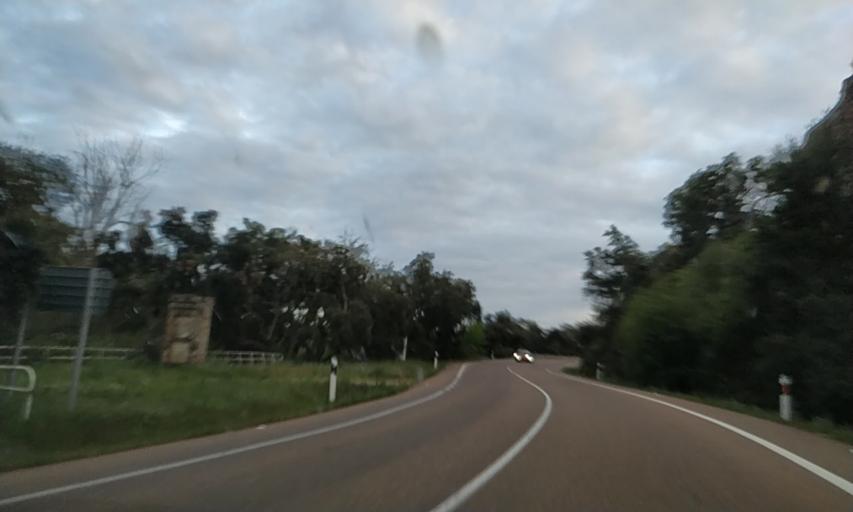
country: ES
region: Extremadura
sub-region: Provincia de Badajoz
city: Puebla de Obando
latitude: 39.1863
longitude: -6.6004
